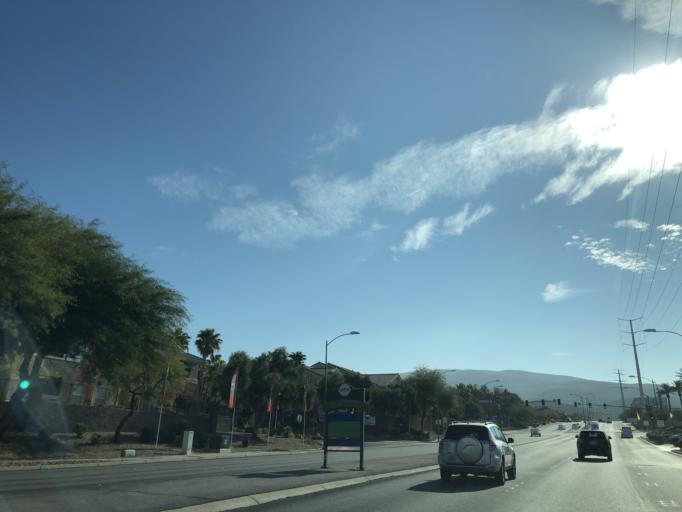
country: US
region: Nevada
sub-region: Clark County
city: Henderson
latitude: 36.0310
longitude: -115.0296
